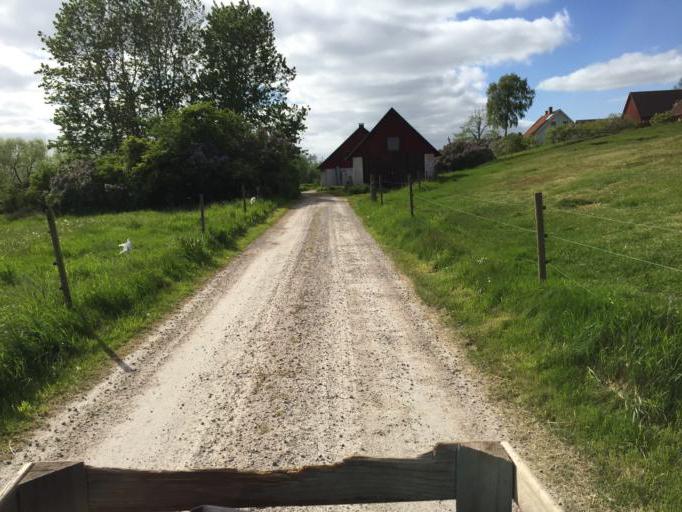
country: SE
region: Skane
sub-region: Sjobo Kommun
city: Sjoebo
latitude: 55.6688
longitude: 13.6267
